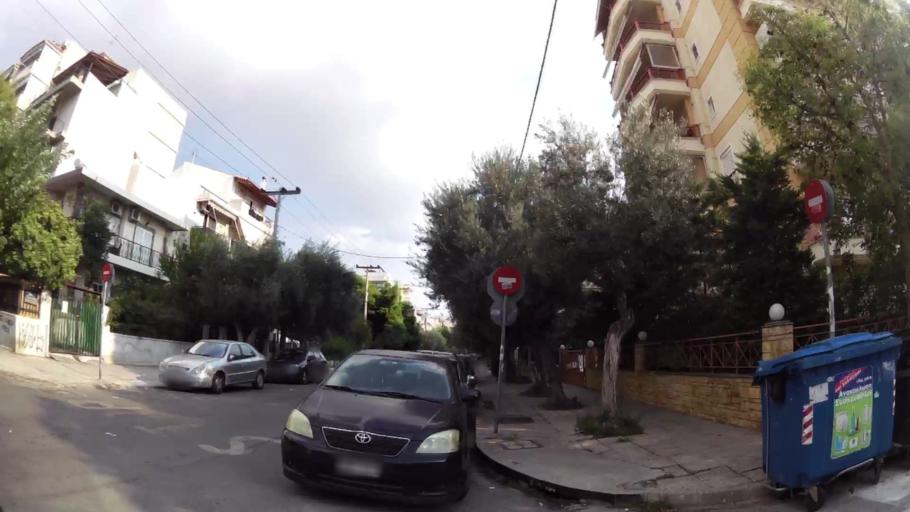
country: GR
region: Attica
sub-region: Nomarchia Athinas
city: Kallithea
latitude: 37.9466
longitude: 23.6912
